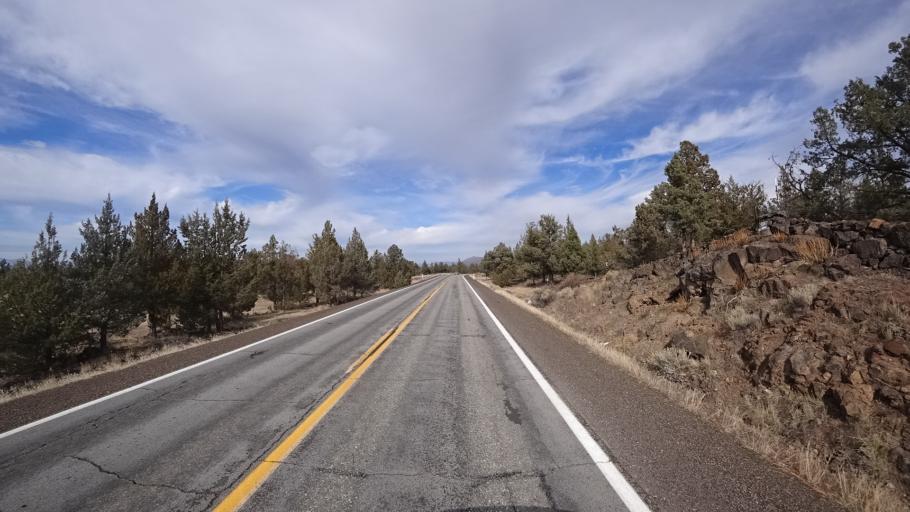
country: US
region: California
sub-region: Siskiyou County
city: Weed
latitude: 41.5997
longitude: -122.3954
